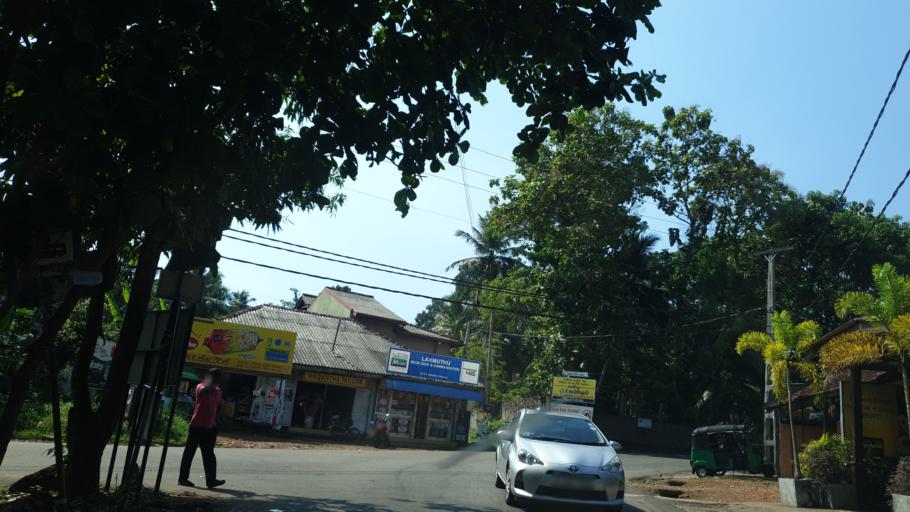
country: LK
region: Western
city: Moratuwa
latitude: 6.7665
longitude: 79.9310
